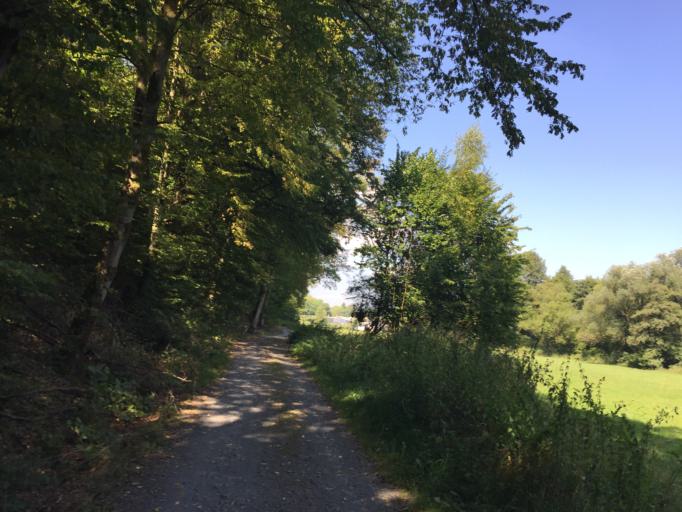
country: DE
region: Hesse
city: Laufdorf
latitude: 50.4910
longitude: 8.4293
